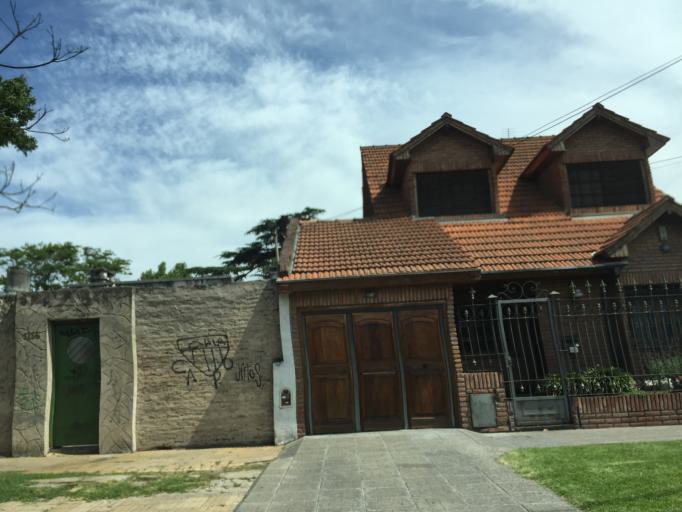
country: AR
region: Buenos Aires
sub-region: Partido de Lomas de Zamora
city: Lomas de Zamora
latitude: -34.7527
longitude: -58.4138
